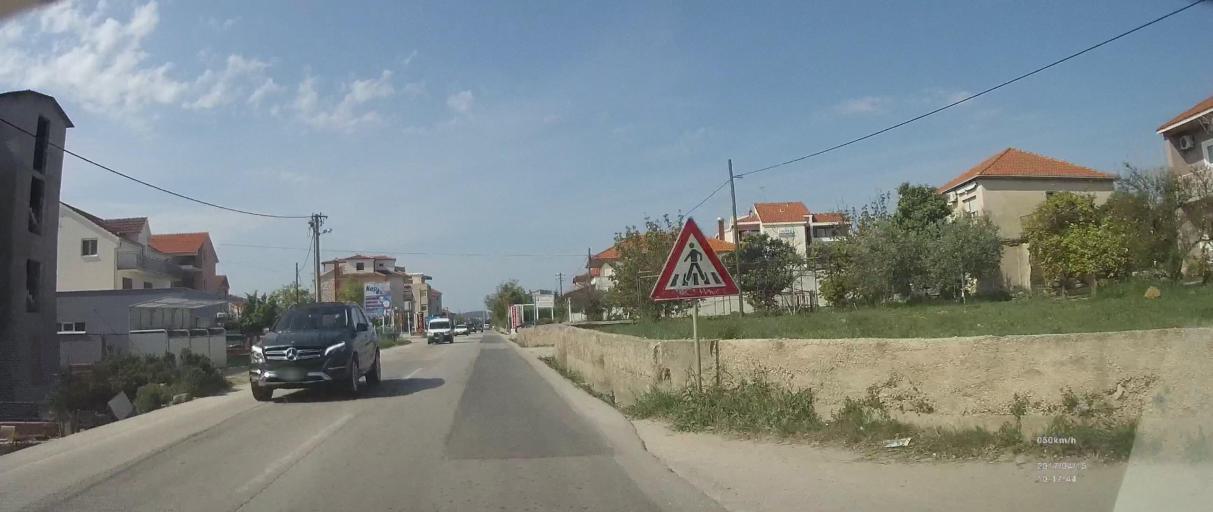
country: HR
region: Splitsko-Dalmatinska
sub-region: Grad Trogir
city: Trogir
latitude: 43.5250
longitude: 16.2681
